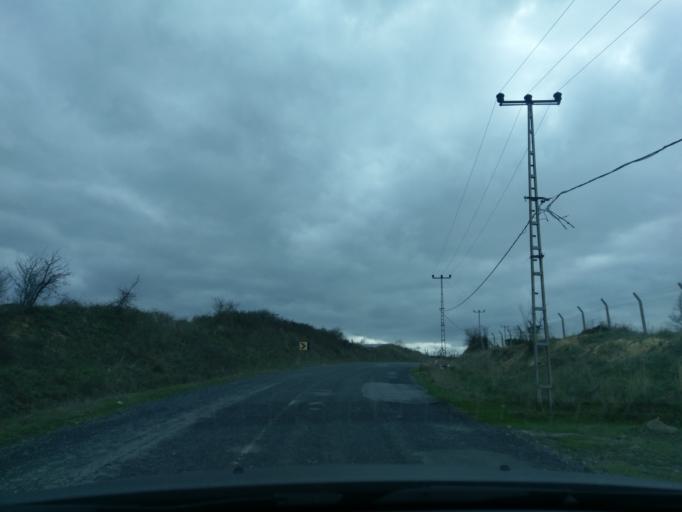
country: TR
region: Istanbul
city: Durusu
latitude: 41.2863
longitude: 28.6926
